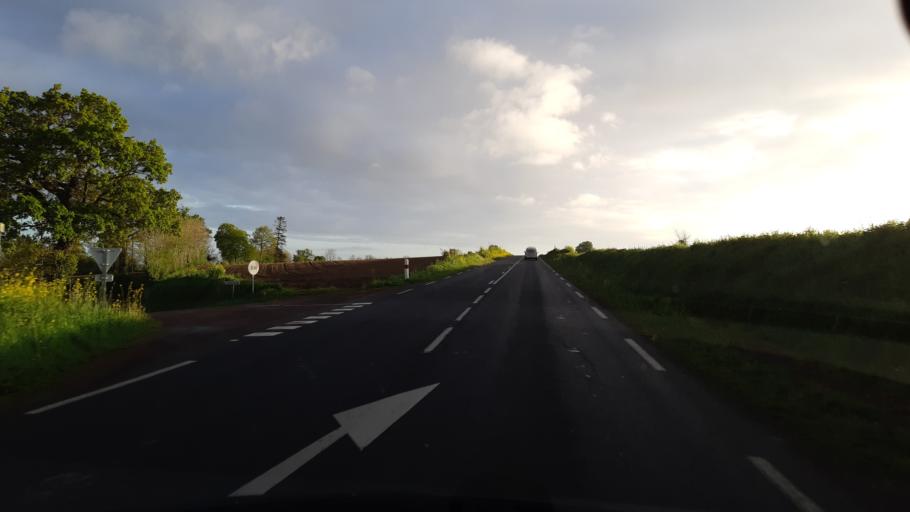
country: FR
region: Lower Normandy
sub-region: Departement de la Manche
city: Agneaux
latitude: 49.0368
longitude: -1.1331
